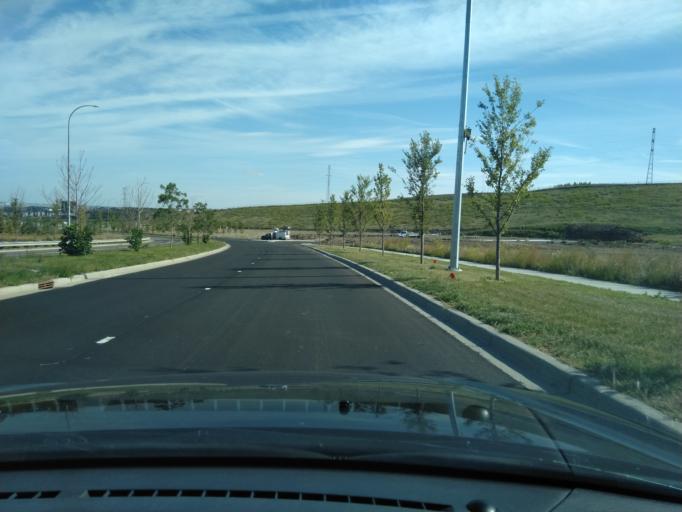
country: CA
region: Alberta
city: Calgary
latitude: 51.1722
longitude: -114.1750
